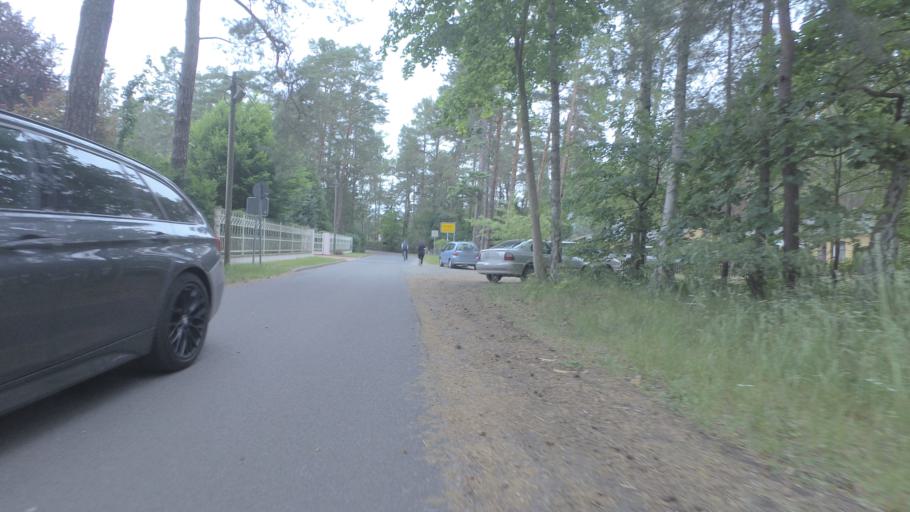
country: DE
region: Brandenburg
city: Bestensee
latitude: 52.2680
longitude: 13.7609
